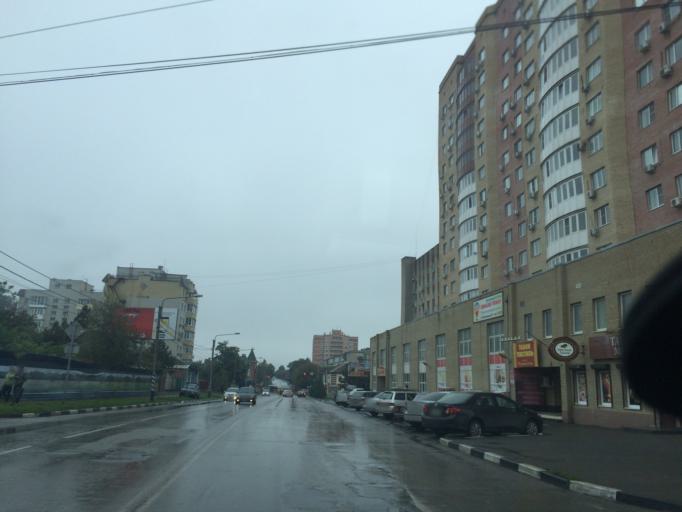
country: RU
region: Rostov
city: Azov
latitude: 47.1074
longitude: 39.4300
